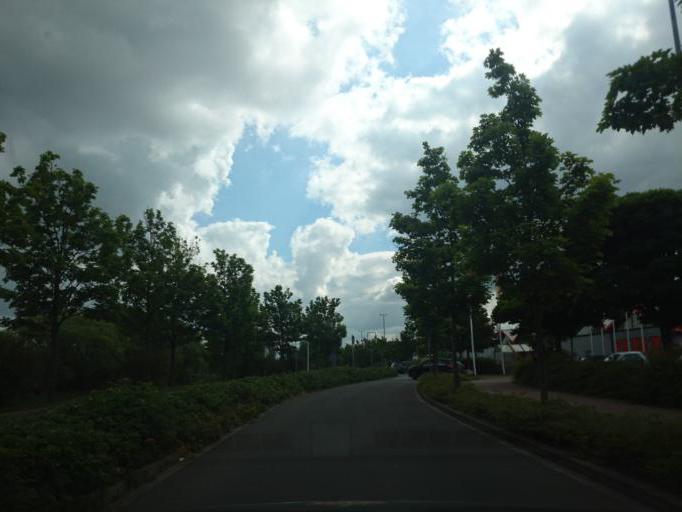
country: DE
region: Brandenburg
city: Rangsdorf
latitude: 52.2999
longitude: 13.4558
